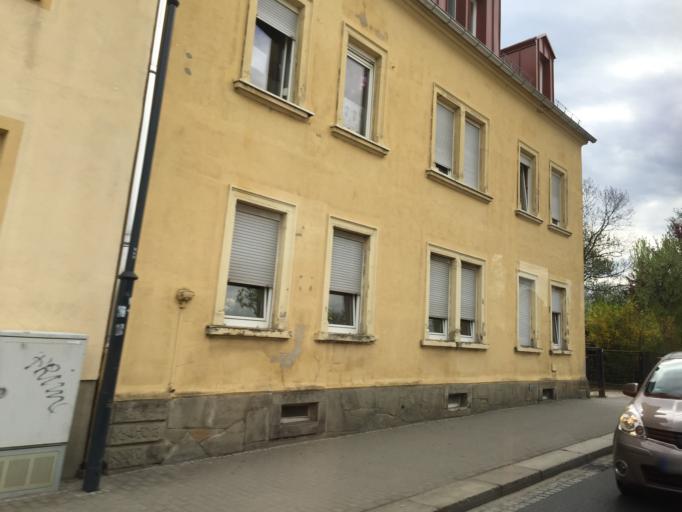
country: DE
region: Saxony
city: Radeberg
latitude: 51.1136
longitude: 13.9167
